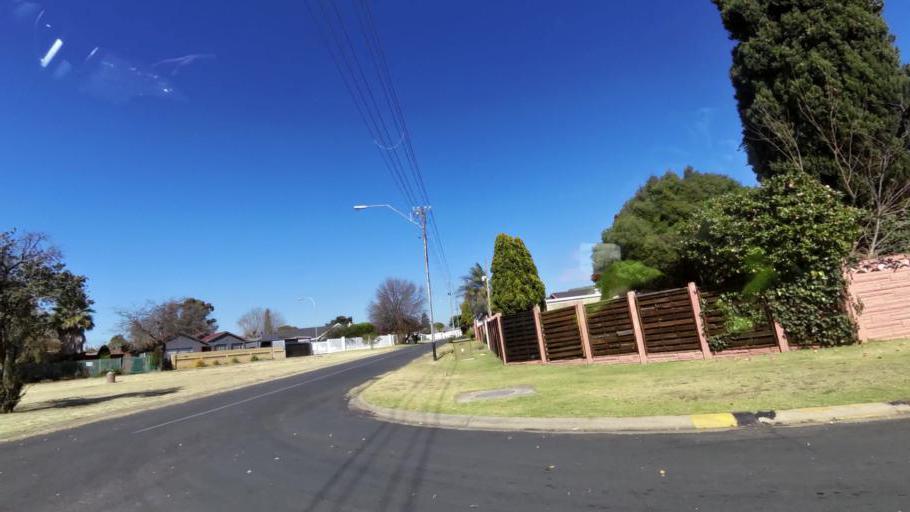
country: ZA
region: Gauteng
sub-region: City of Johannesburg Metropolitan Municipality
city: Johannesburg
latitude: -26.2436
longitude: 28.0014
